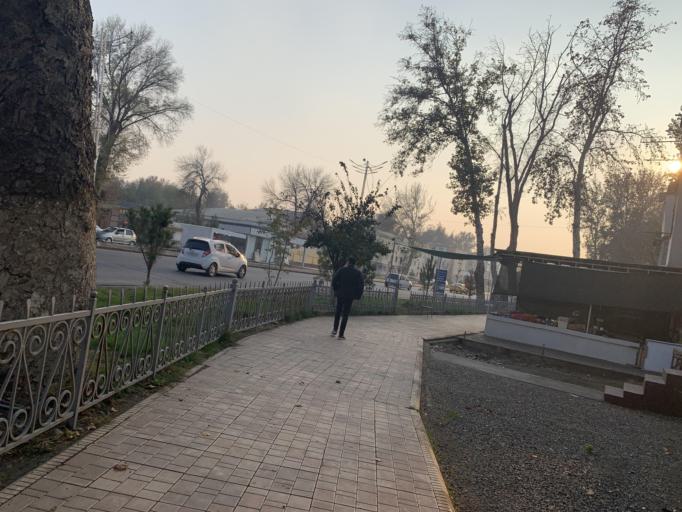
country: UZ
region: Fergana
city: Qo`qon
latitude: 40.5270
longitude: 70.9394
